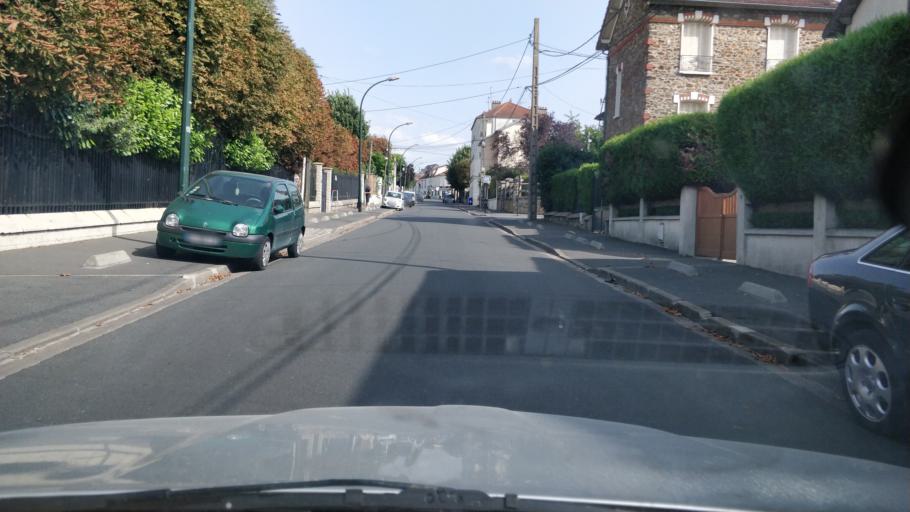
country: FR
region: Ile-de-France
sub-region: Departement de Seine-Saint-Denis
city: Le Raincy
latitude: 48.8966
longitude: 2.5203
